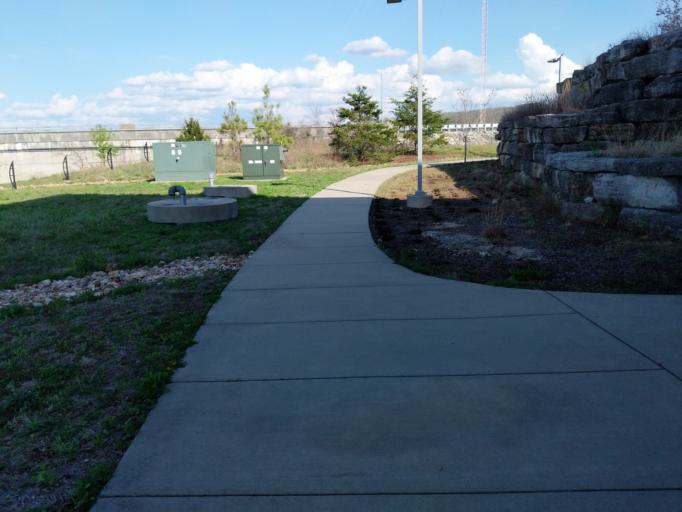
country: US
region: Missouri
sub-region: Taney County
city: Hollister
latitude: 36.5940
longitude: -93.3122
